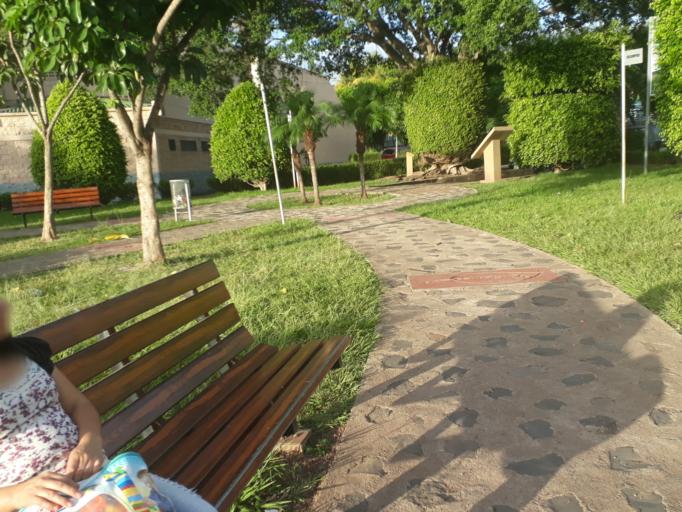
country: HN
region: Francisco Morazan
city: Tegucigalpa
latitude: 14.0903
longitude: -87.1625
